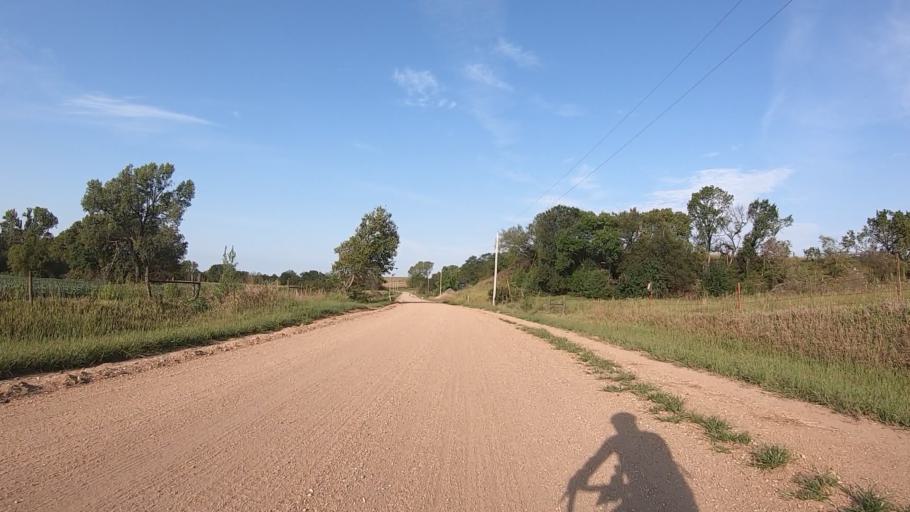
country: US
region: Kansas
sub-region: Marshall County
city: Blue Rapids
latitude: 39.6731
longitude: -96.8008
